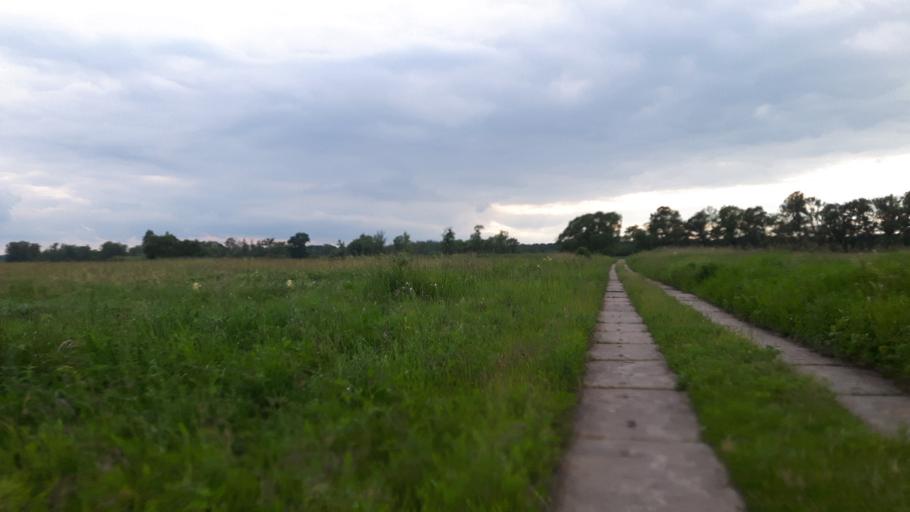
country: PL
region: West Pomeranian Voivodeship
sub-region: Powiat gryfinski
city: Widuchowa
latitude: 53.1390
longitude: 14.3675
